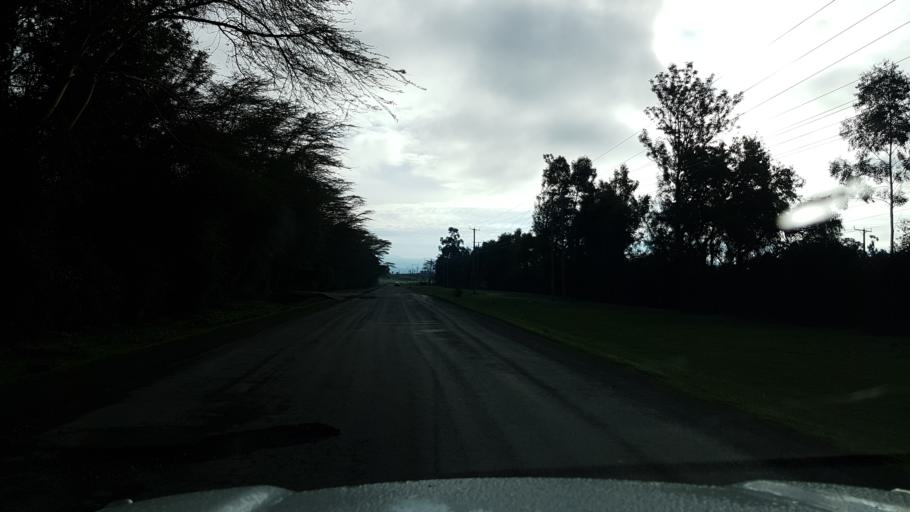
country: KE
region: Nakuru
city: Naivasha
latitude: -0.8255
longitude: 36.3786
